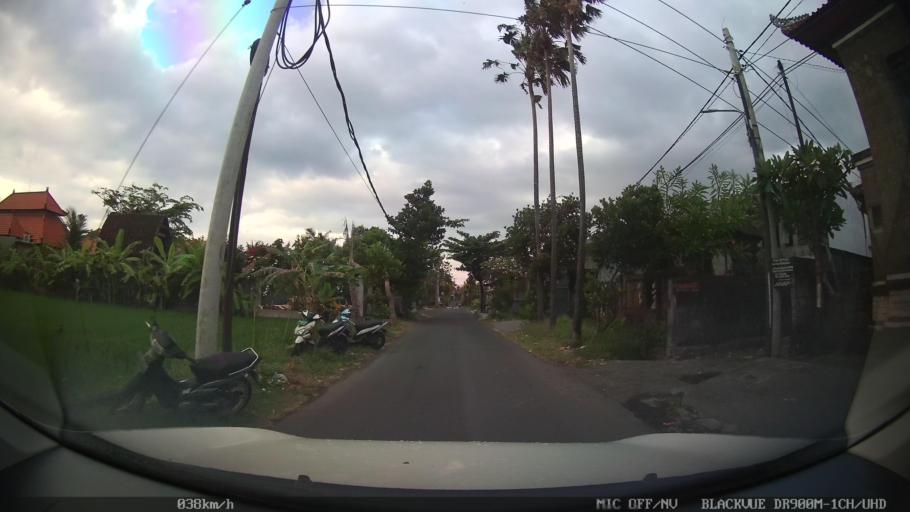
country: ID
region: Bali
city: Banjar Pasekan
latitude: -8.6396
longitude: 115.2821
